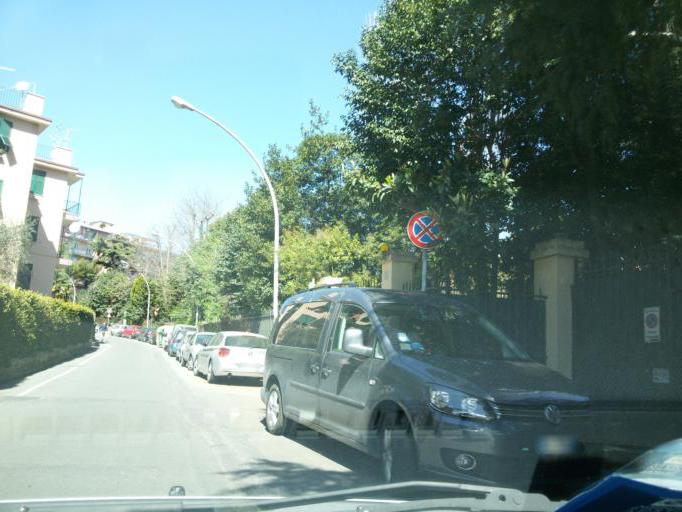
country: IT
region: Liguria
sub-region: Provincia di Genova
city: Bogliasco
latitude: 44.3910
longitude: 9.0016
